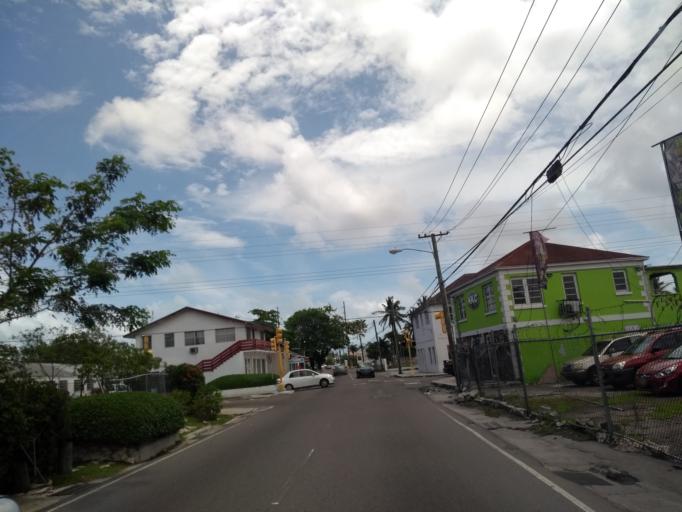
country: BS
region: New Providence
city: Nassau
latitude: 25.0730
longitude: -77.3232
